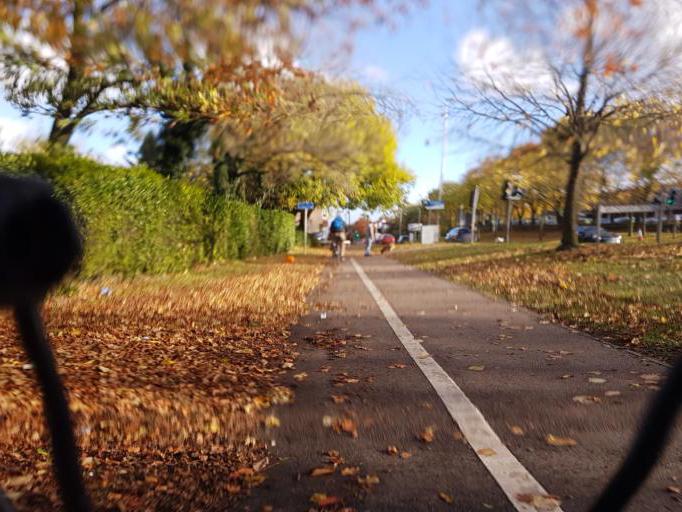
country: GB
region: England
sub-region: Kent
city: Rainham
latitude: 51.3686
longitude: 0.5823
